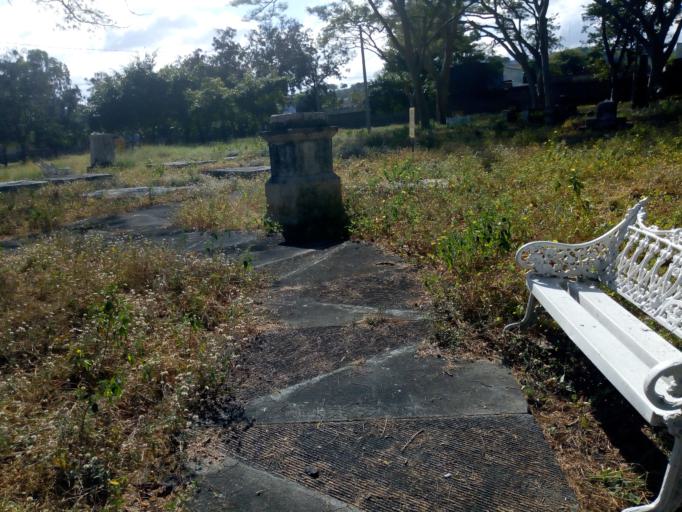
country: NI
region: Managua
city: Managua
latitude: 12.1473
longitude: -86.2762
